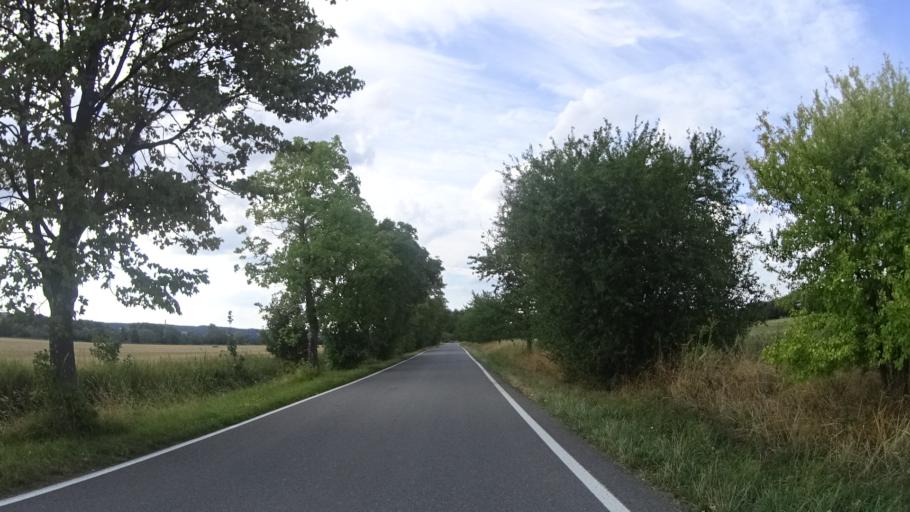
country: CZ
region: Olomoucky
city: Dubicko
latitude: 49.8195
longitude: 16.9391
